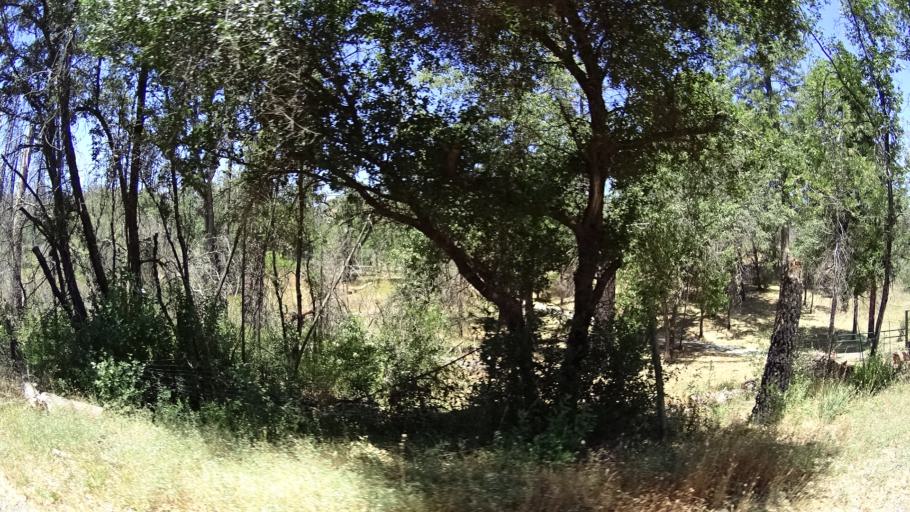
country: US
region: California
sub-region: Calaveras County
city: Mountain Ranch
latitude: 38.2363
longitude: -120.5790
